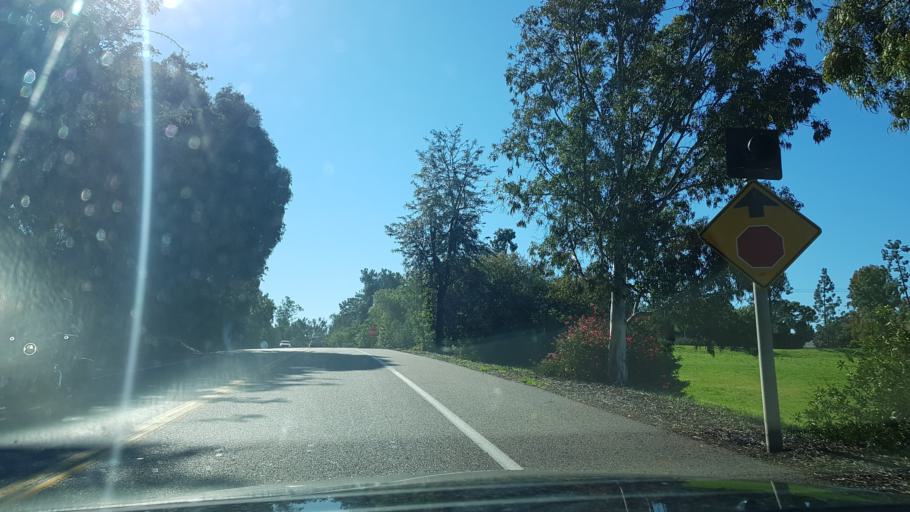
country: US
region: California
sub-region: San Diego County
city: Rancho Santa Fe
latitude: 33.0314
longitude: -117.1902
